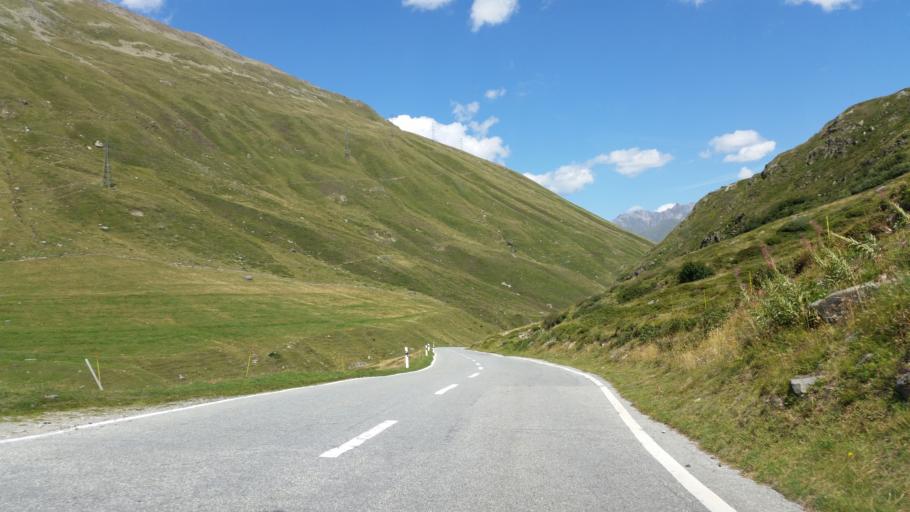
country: IT
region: Aosta Valley
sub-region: Valle d'Aosta
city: San Leonardo
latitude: 45.8931
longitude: 7.1865
